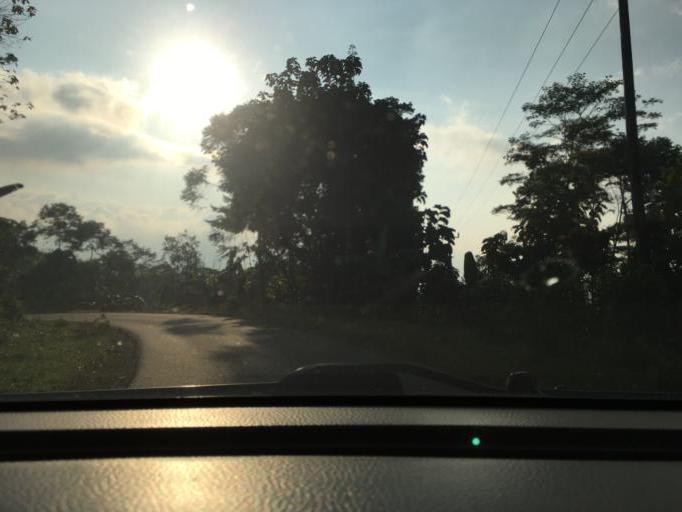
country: ID
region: West Java
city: Maniis
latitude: -7.0372
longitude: 108.3214
